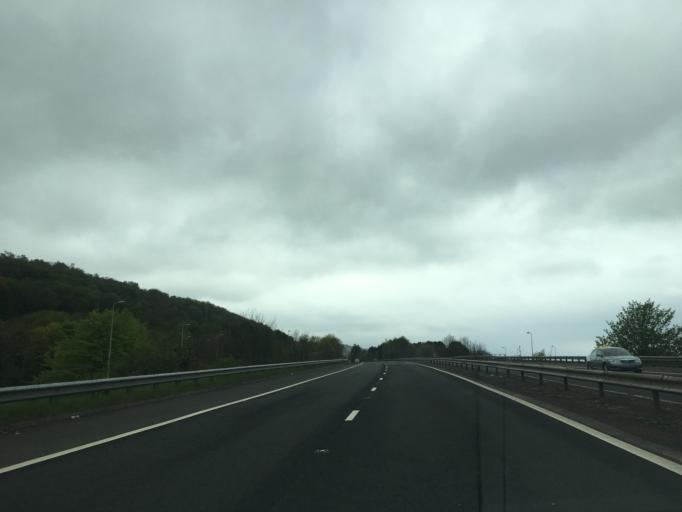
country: GB
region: Scotland
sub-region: West Dunbartonshire
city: Dumbarton
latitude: 55.9235
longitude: -4.5532
